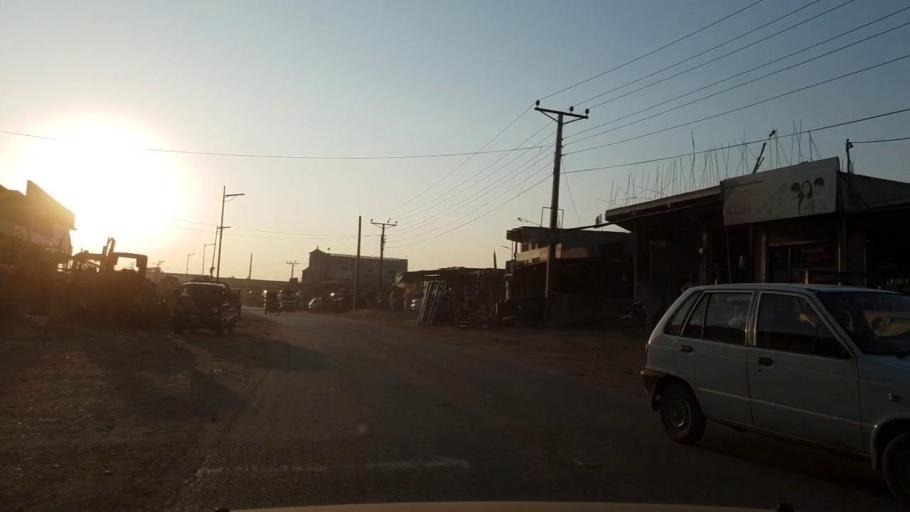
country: PK
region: Sindh
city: Thatta
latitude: 24.6069
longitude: 68.0724
